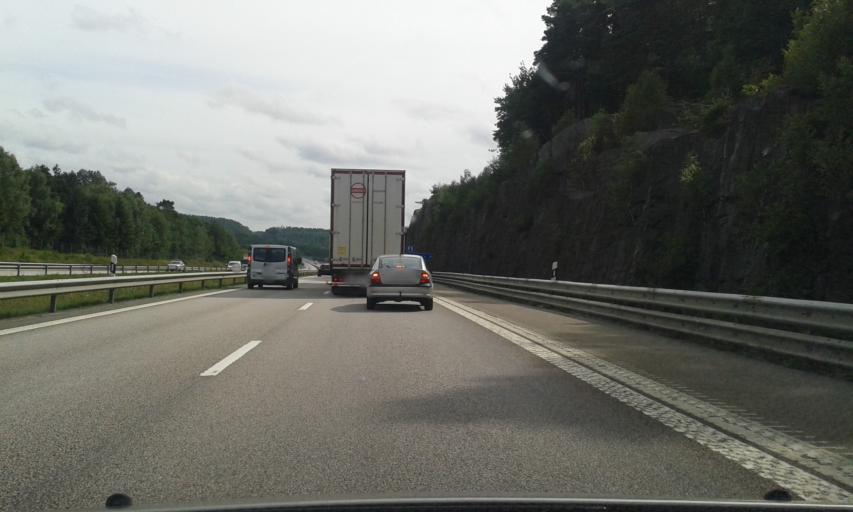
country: SE
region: Halland
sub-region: Kungsbacka Kommun
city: Frillesas
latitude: 57.3335
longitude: 12.2058
